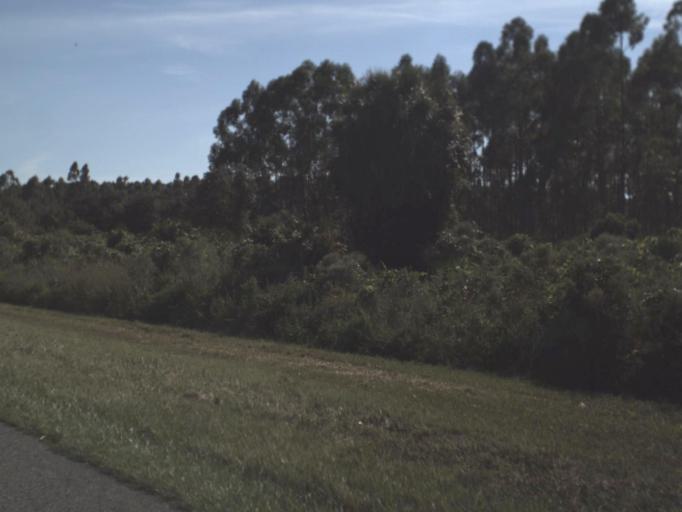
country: US
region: Florida
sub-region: Hendry County
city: Port LaBelle
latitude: 26.9883
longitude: -81.3246
